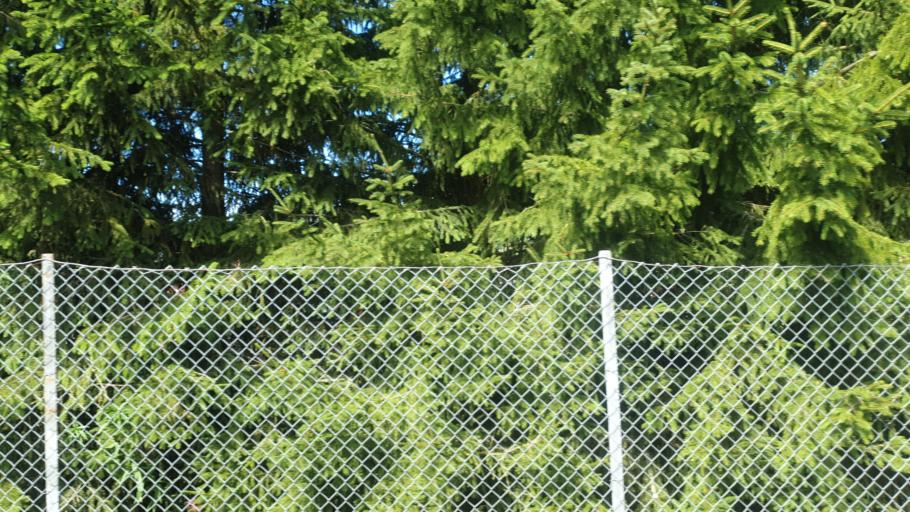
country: NO
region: Sor-Trondelag
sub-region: Orkdal
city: Orkanger
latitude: 63.2770
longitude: 9.8251
